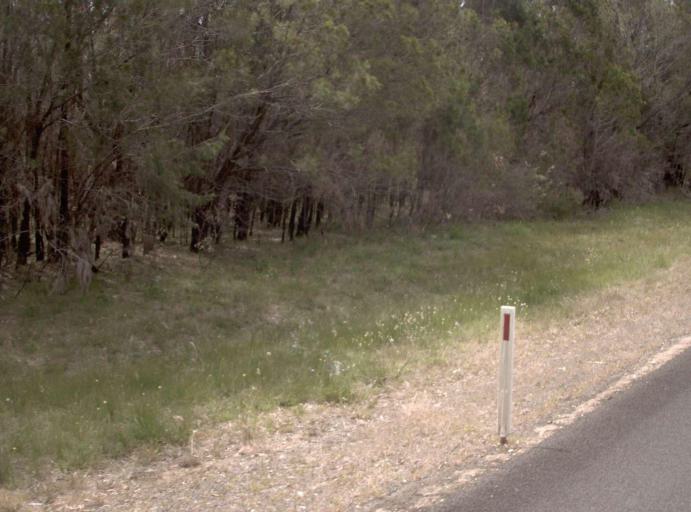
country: AU
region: New South Wales
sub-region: Bega Valley
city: Eden
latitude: -37.5191
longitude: 149.4968
